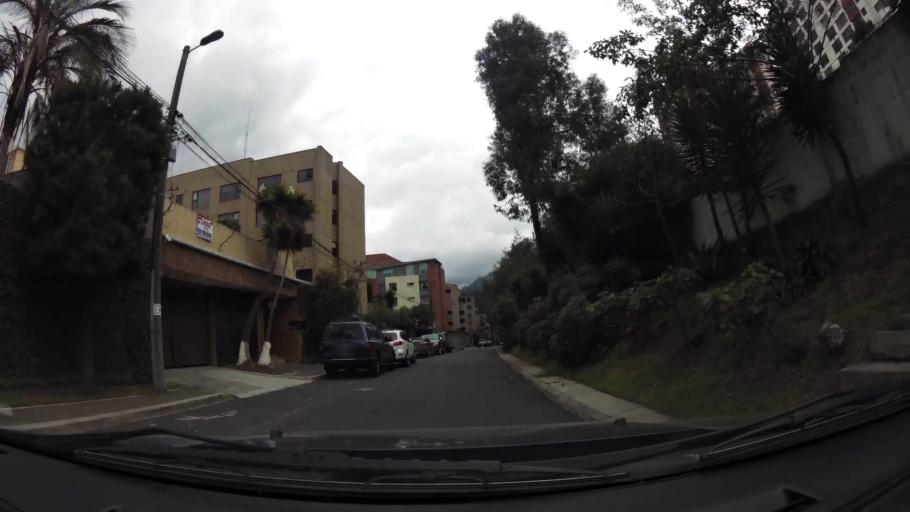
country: EC
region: Pichincha
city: Quito
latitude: -0.1660
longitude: -78.4961
